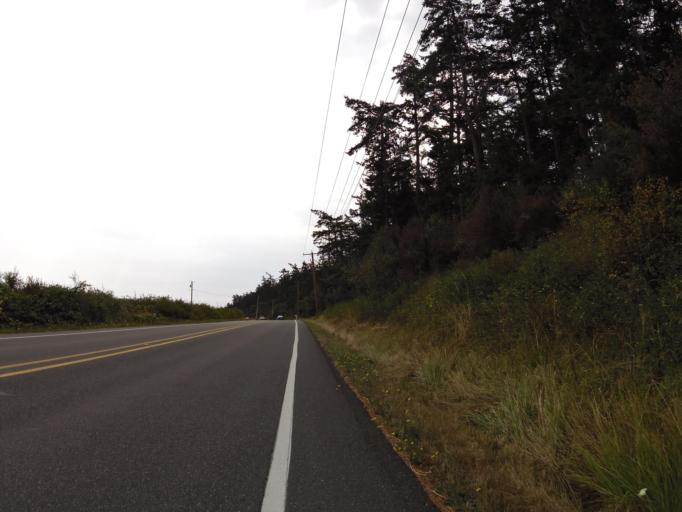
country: US
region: Washington
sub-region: Island County
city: Coupeville
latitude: 48.1858
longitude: -122.6690
